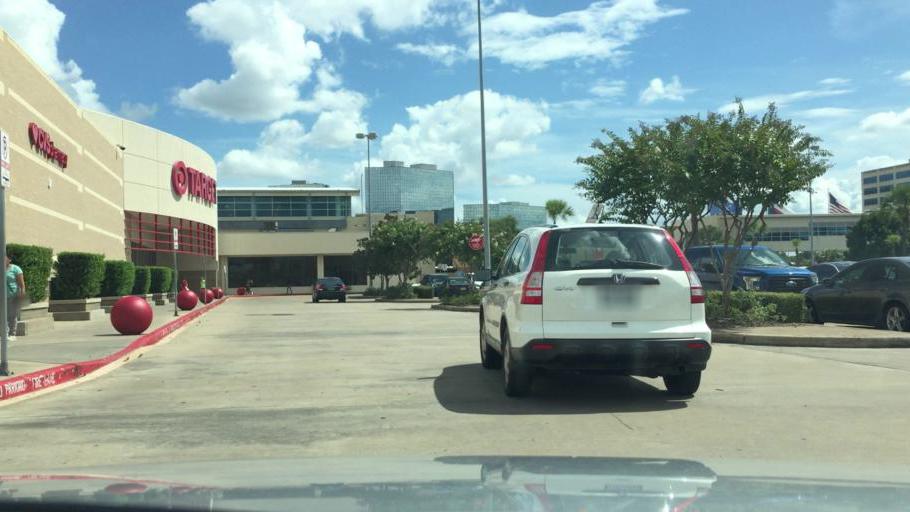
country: US
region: Texas
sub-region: Harris County
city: Bunker Hill Village
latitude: 29.7832
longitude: -95.5424
